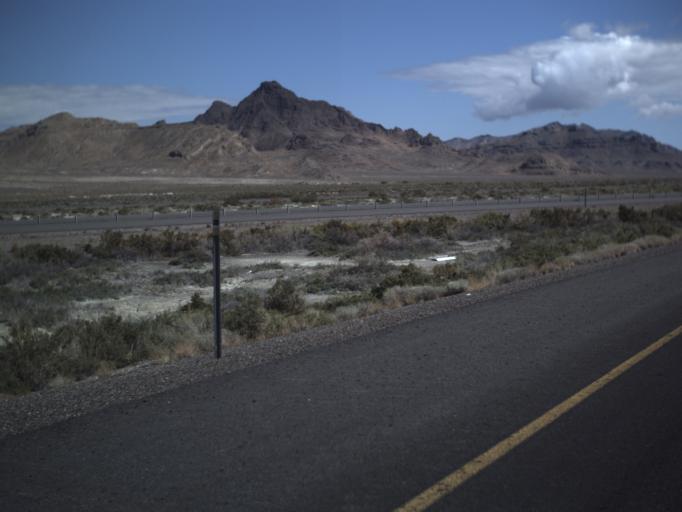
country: US
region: Utah
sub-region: Tooele County
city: Wendover
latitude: 40.7452
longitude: -114.0162
